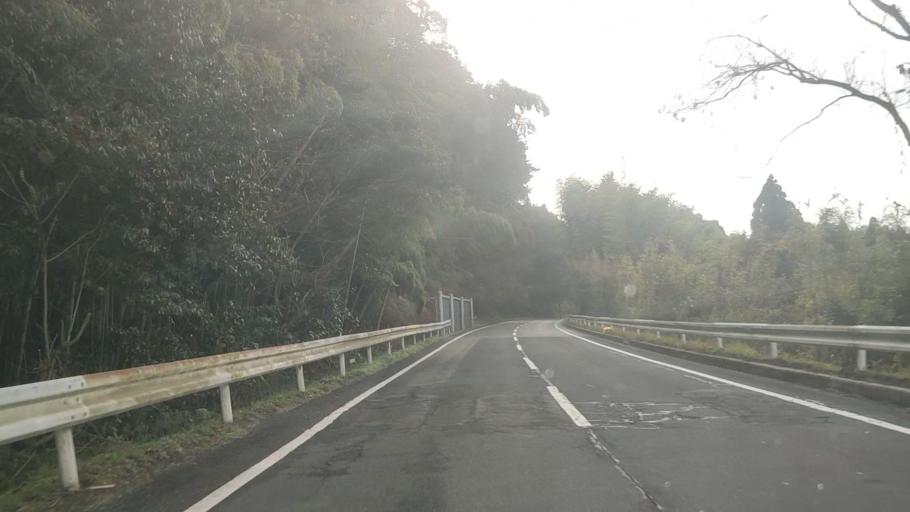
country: JP
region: Kagoshima
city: Okuchi-shinohara
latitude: 31.9682
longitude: 130.7400
